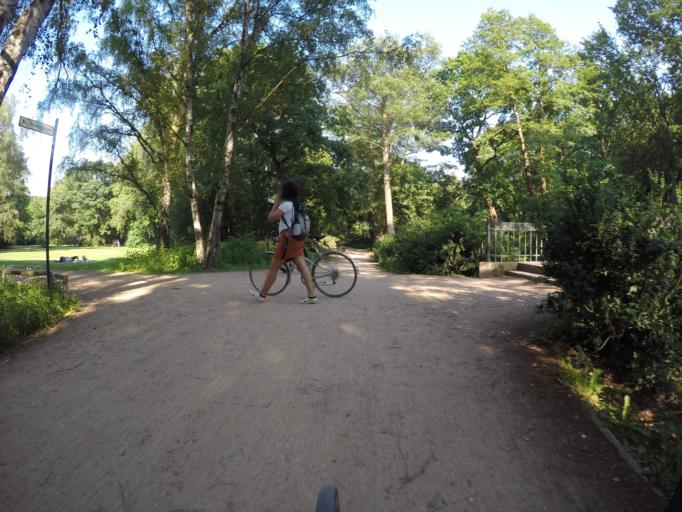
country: DE
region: Berlin
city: Tiergarten Bezirk
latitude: 52.5125
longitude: 13.3601
